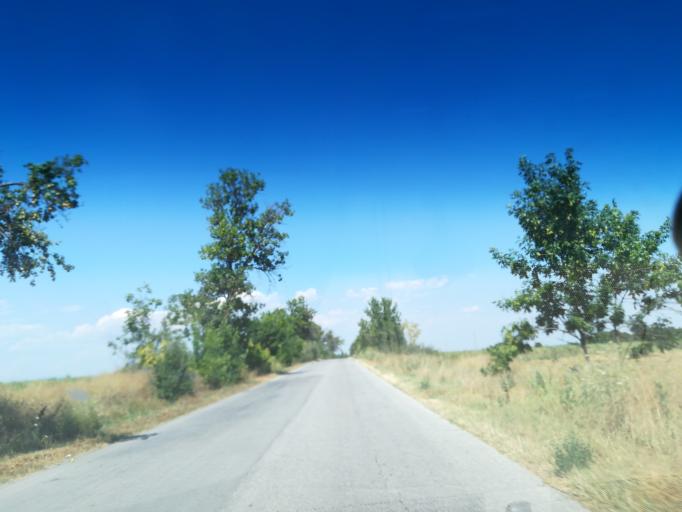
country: BG
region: Stara Zagora
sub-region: Obshtina Chirpan
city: Chirpan
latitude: 42.0561
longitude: 25.1539
